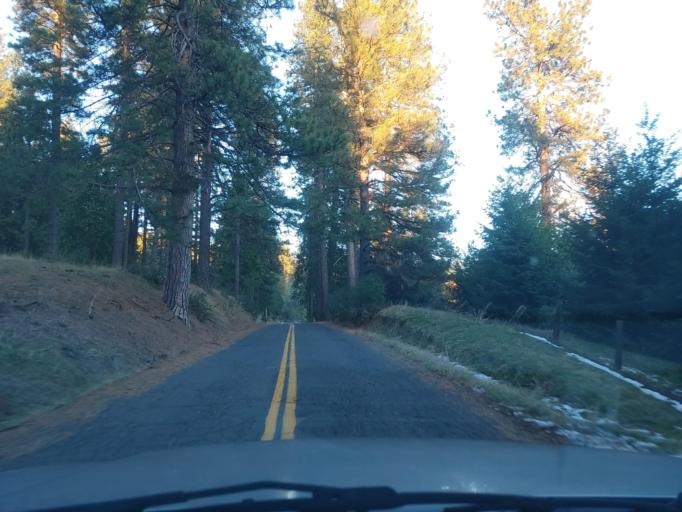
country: US
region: California
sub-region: Tuolumne County
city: Cedar Ridge
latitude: 38.0410
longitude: -120.3037
